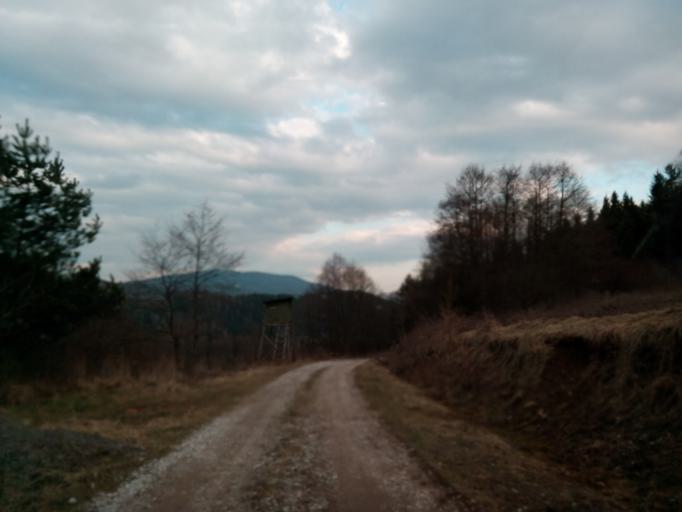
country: SK
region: Kosicky
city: Krompachy
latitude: 48.9525
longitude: 20.8947
